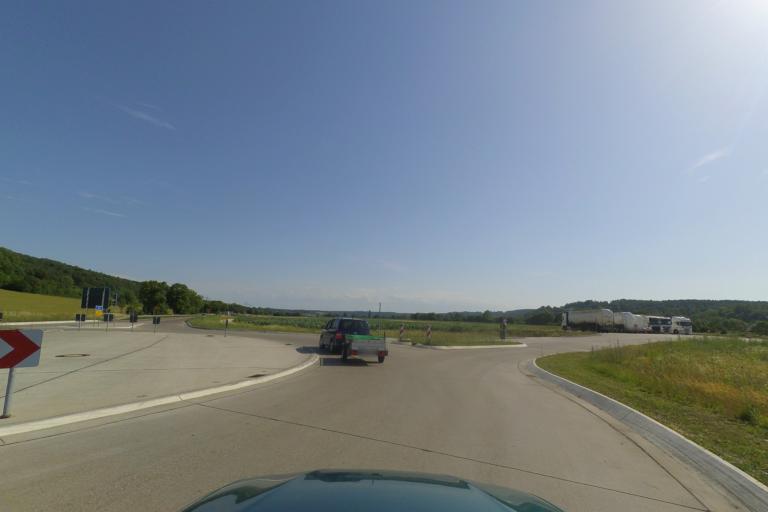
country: DE
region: Baden-Wuerttemberg
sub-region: Regierungsbezirk Stuttgart
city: Bolheim
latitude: 48.6498
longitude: 10.1651
